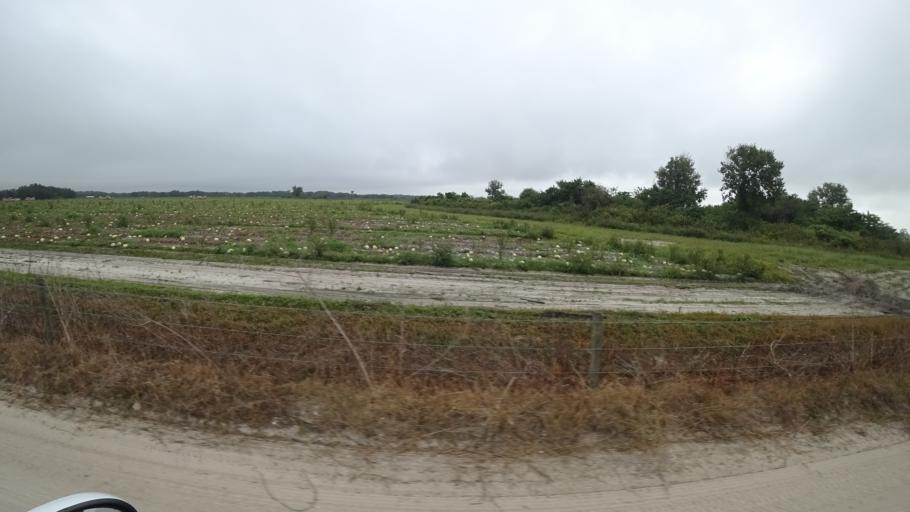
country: US
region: Florida
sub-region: Sarasota County
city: Warm Mineral Springs
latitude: 27.2782
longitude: -82.1699
